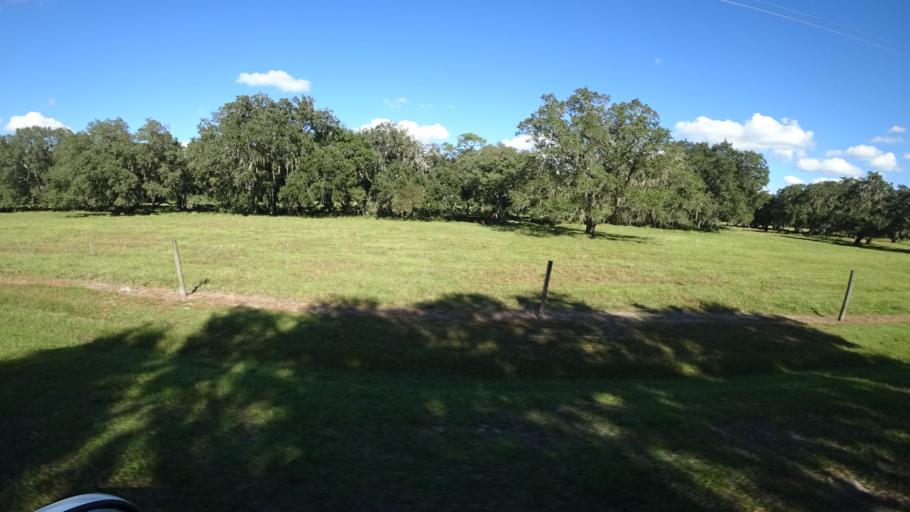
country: US
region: Florida
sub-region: Sarasota County
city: Lake Sarasota
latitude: 27.2843
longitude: -82.2149
